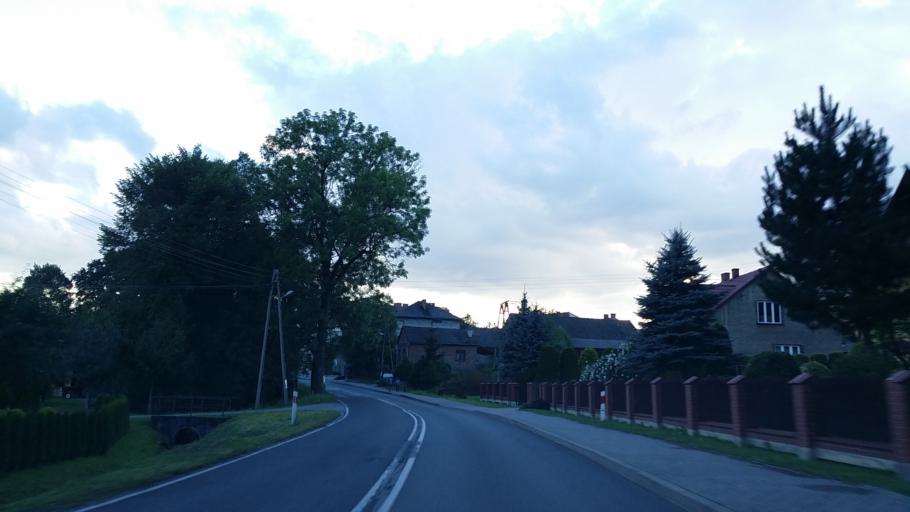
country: PL
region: Lesser Poland Voivodeship
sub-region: Powiat oswiecimski
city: Polanka Wielka
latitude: 49.9851
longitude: 19.3199
